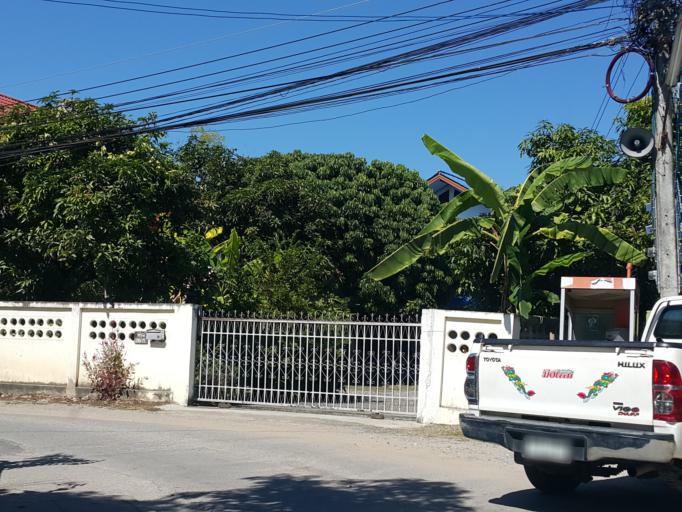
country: TH
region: Chiang Mai
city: San Sai
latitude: 18.8103
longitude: 99.0597
